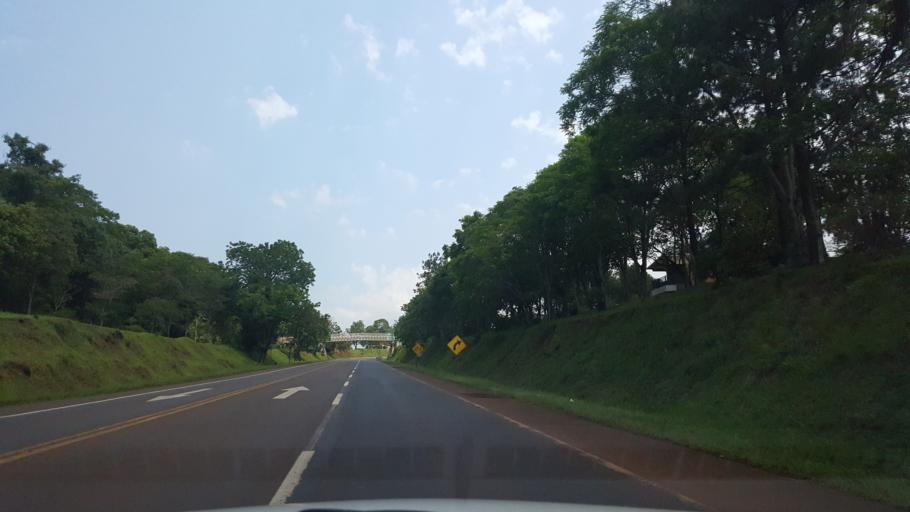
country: AR
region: Misiones
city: Capiovi
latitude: -26.9299
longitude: -55.0603
